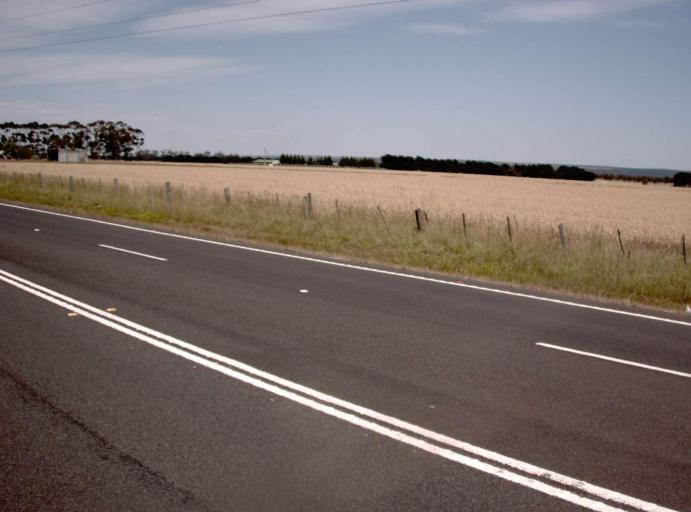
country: AU
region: Victoria
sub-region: Wellington
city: Sale
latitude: -38.1031
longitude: 146.9334
